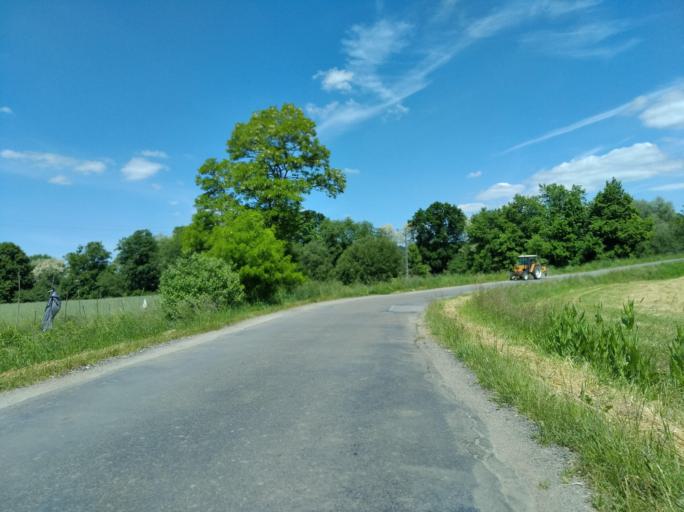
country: PL
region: Subcarpathian Voivodeship
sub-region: Powiat krosnienski
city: Wojaszowka
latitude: 49.7841
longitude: 21.6799
